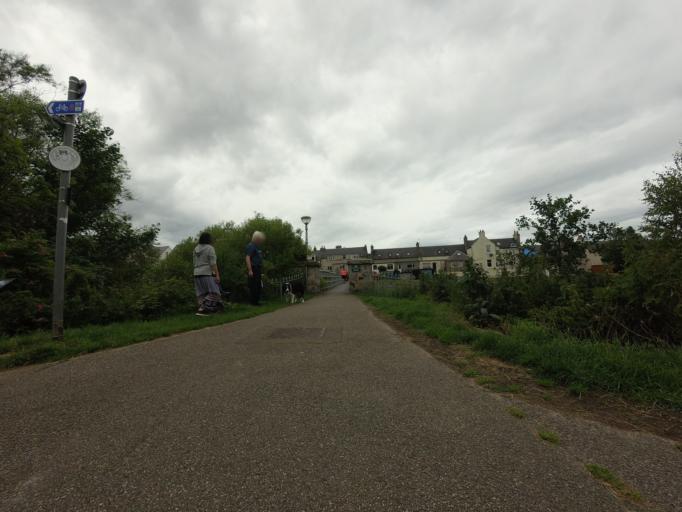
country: GB
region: Scotland
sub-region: Highland
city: Nairn
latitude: 57.5865
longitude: -3.8633
